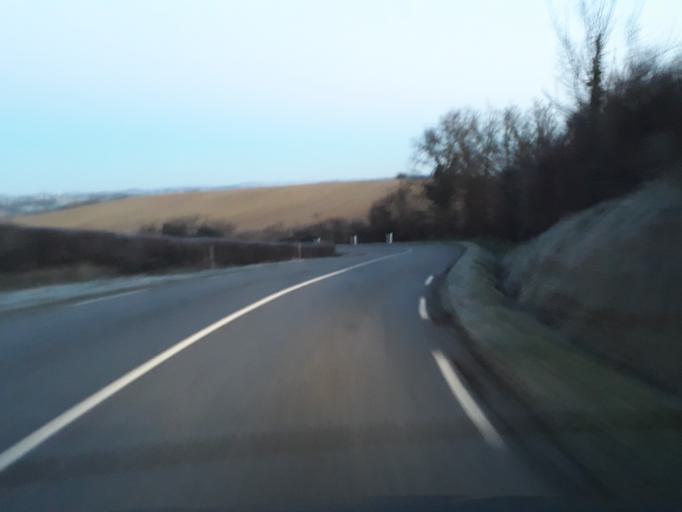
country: FR
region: Midi-Pyrenees
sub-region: Departement du Gers
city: Samatan
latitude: 43.4717
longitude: 0.9645
